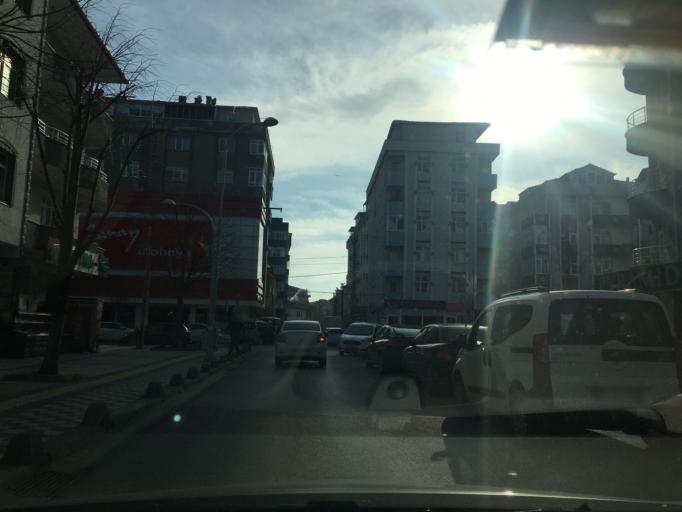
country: TR
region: Tekirdag
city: Cerkezkoey
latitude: 41.2894
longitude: 27.9980
